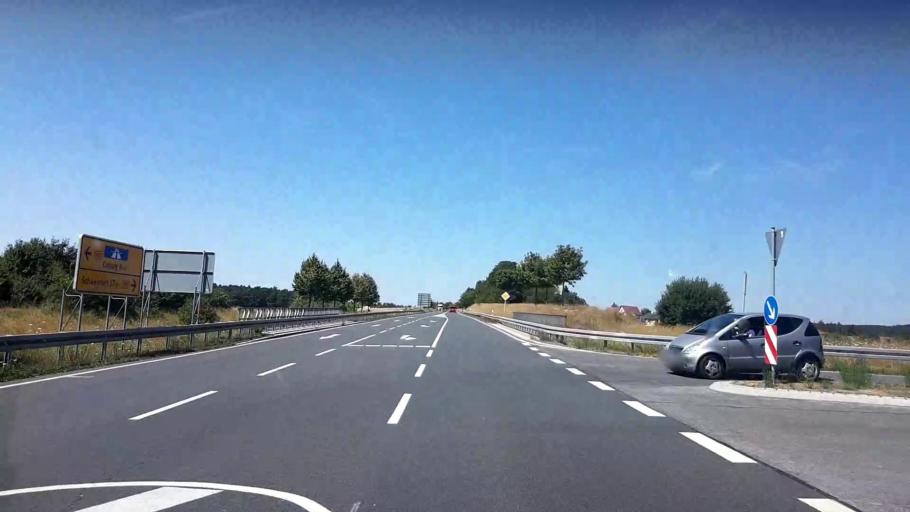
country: DE
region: Bavaria
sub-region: Upper Franconia
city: Ahorn
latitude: 50.2335
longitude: 10.9190
